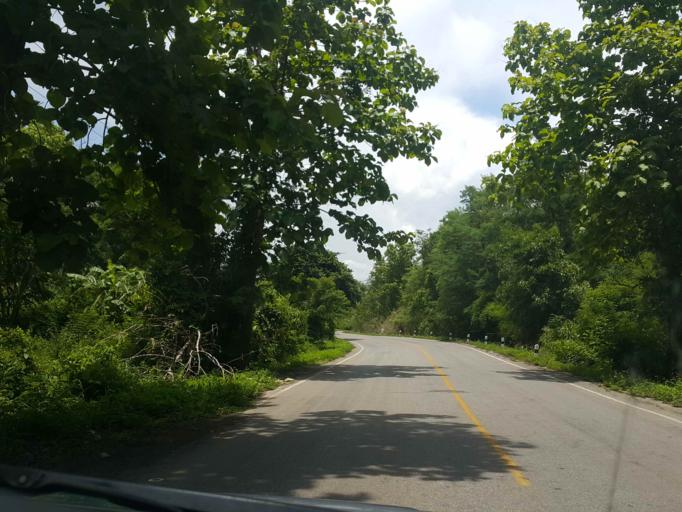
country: TH
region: Phayao
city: Chiang Muan
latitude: 18.9235
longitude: 100.2125
